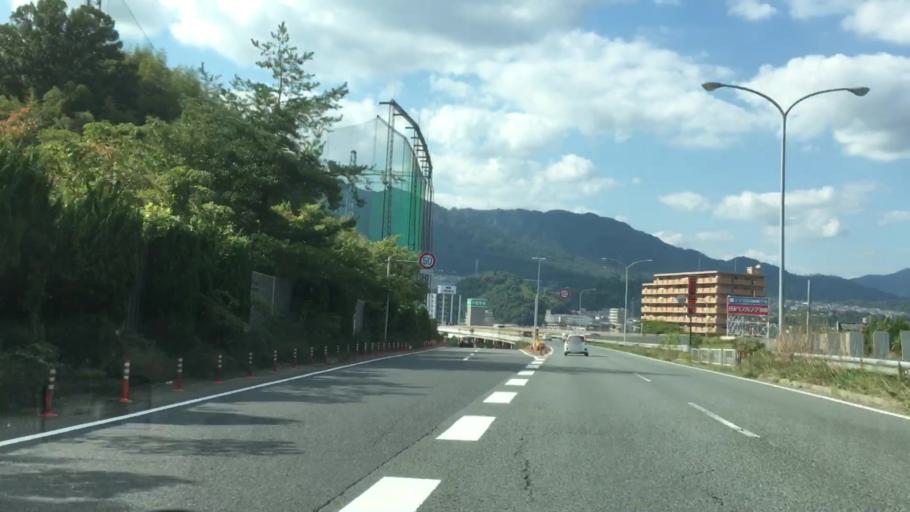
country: JP
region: Hiroshima
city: Hatsukaichi
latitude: 34.3781
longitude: 132.3654
